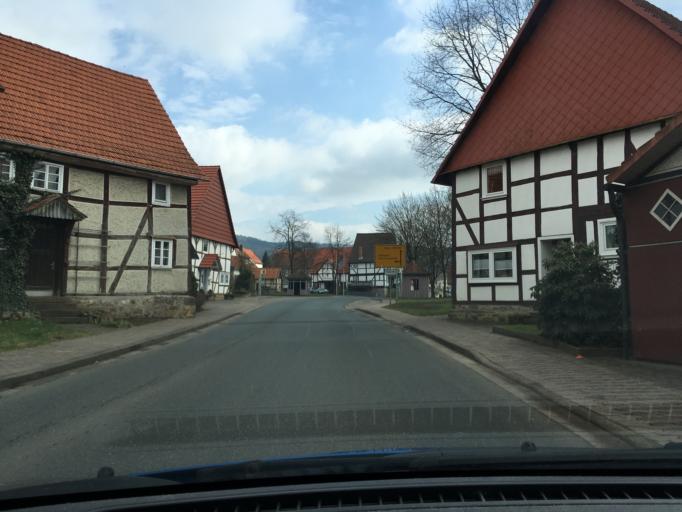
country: DE
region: Lower Saxony
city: Bodenfelde
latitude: 51.5911
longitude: 9.5945
